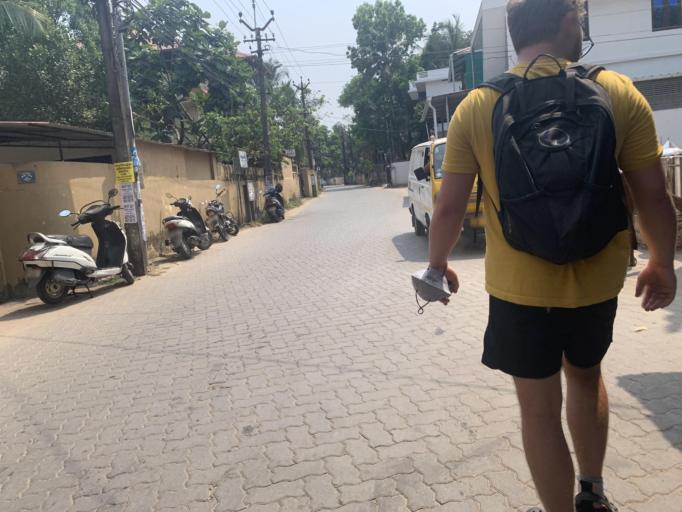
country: IN
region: Kerala
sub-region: Ernakulam
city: Cochin
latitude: 9.9348
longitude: 76.3099
